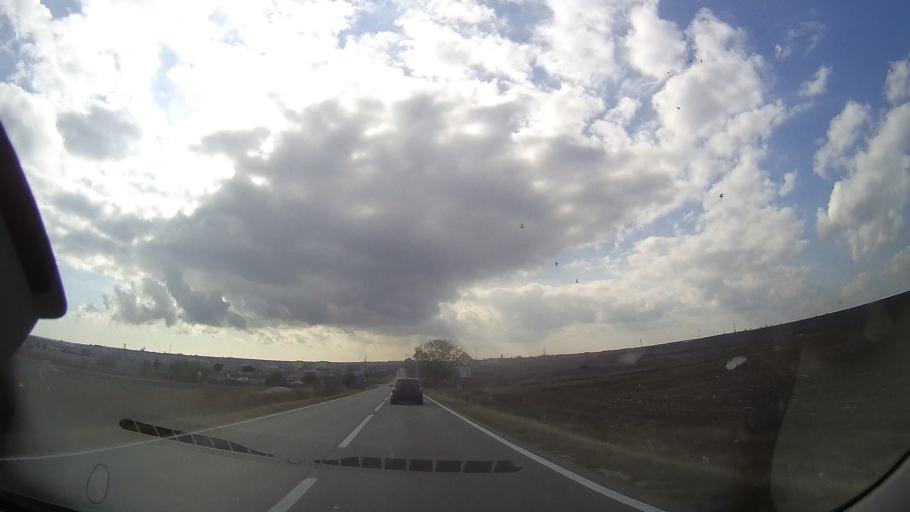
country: RO
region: Constanta
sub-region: Oras Techirghiol
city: Techirghiol
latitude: 44.0670
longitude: 28.5942
